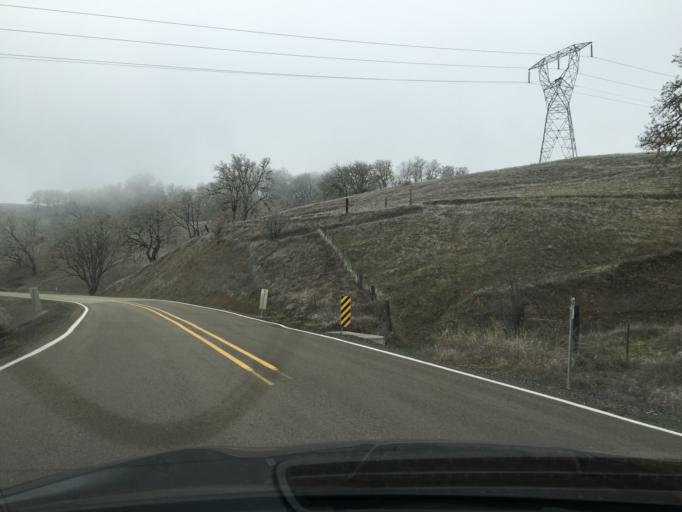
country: US
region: Oregon
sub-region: Douglas County
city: Sutherlin
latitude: 43.3685
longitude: -123.4552
